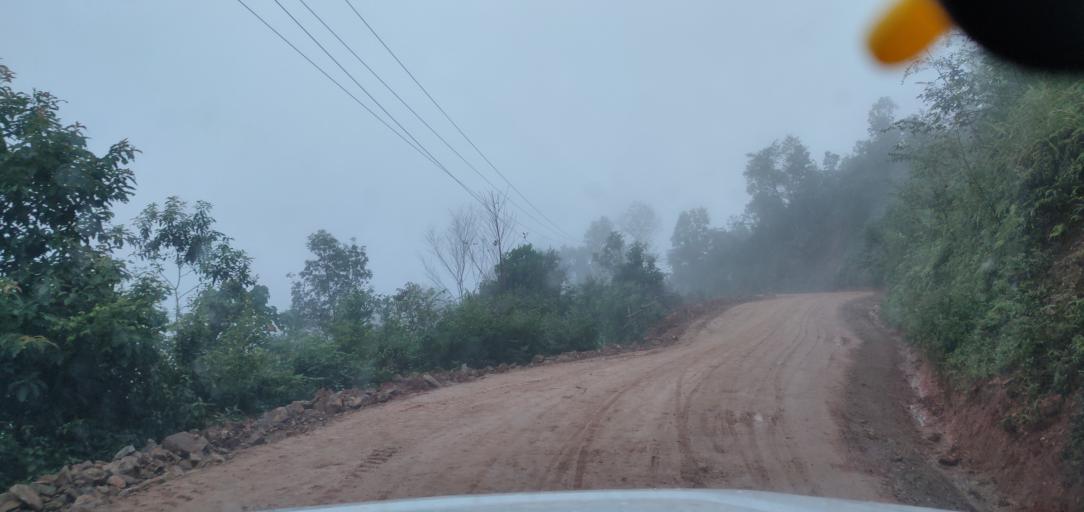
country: LA
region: Phongsali
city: Phongsali
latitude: 21.4288
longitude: 102.2598
